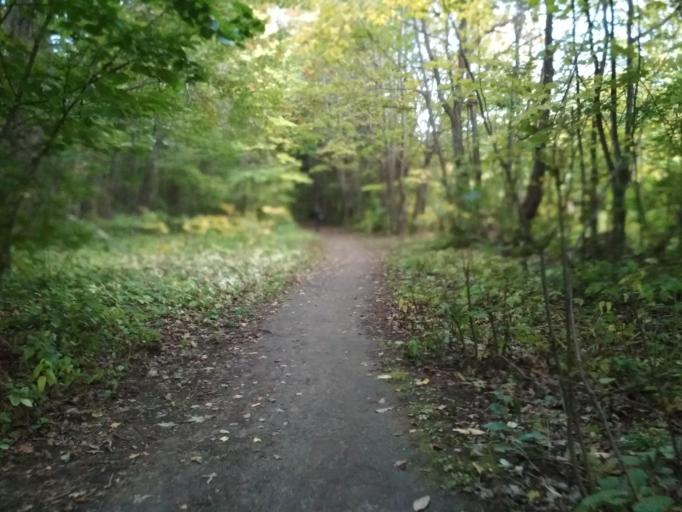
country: RU
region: Chuvashia
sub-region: Cheboksarskiy Rayon
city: Cheboksary
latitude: 56.1361
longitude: 47.1779
